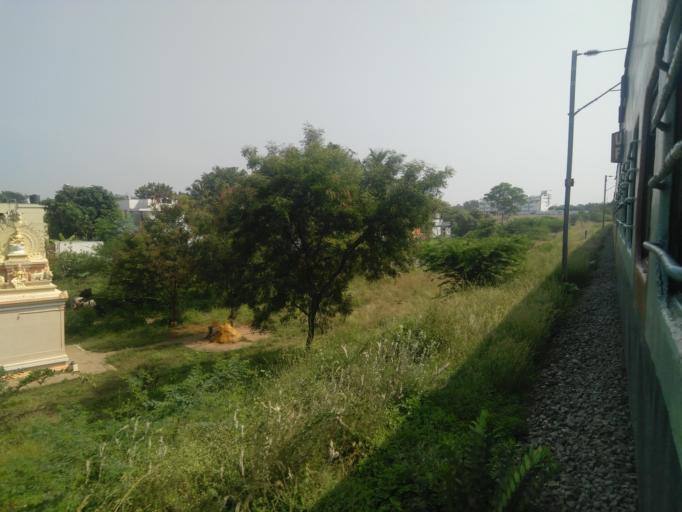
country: IN
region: Tamil Nadu
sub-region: Coimbatore
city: Karamadai
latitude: 11.2667
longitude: 76.9485
